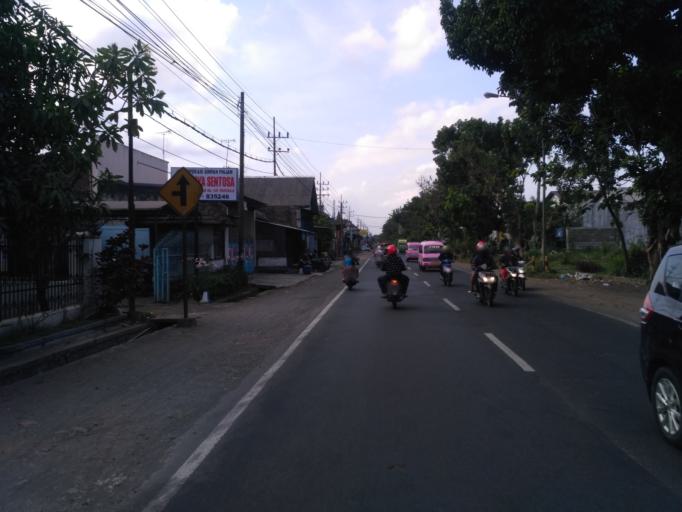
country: ID
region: East Java
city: Pakisaji
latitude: -8.0601
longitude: 112.6015
